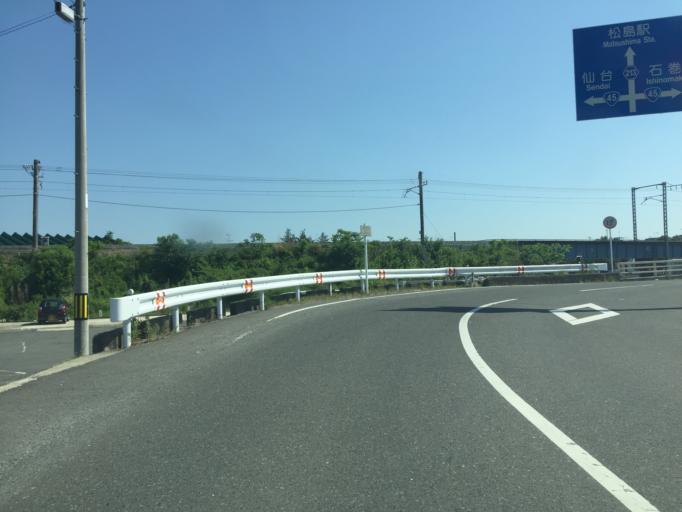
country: JP
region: Miyagi
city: Matsushima
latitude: 38.3798
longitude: 141.0693
